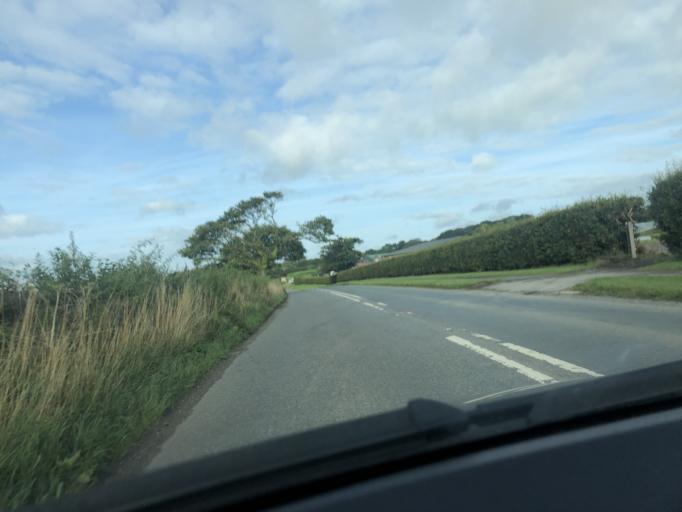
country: GB
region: England
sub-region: Cornwall
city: Launceston
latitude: 50.6450
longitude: -4.2948
